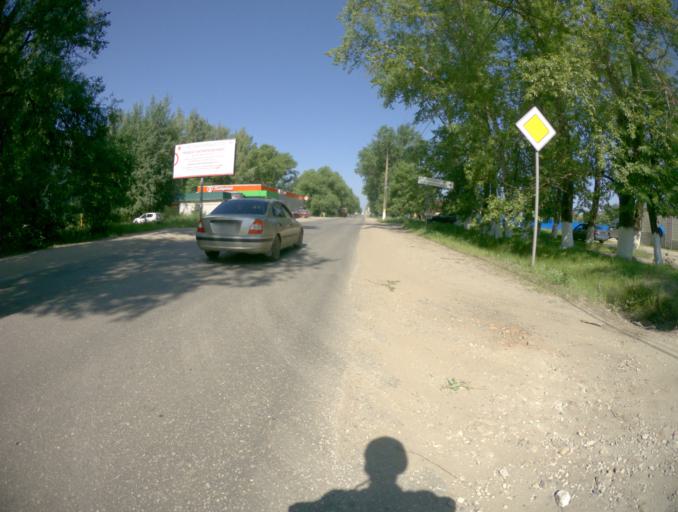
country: RU
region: Vladimir
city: Vyazniki
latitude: 56.2324
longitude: 42.1947
